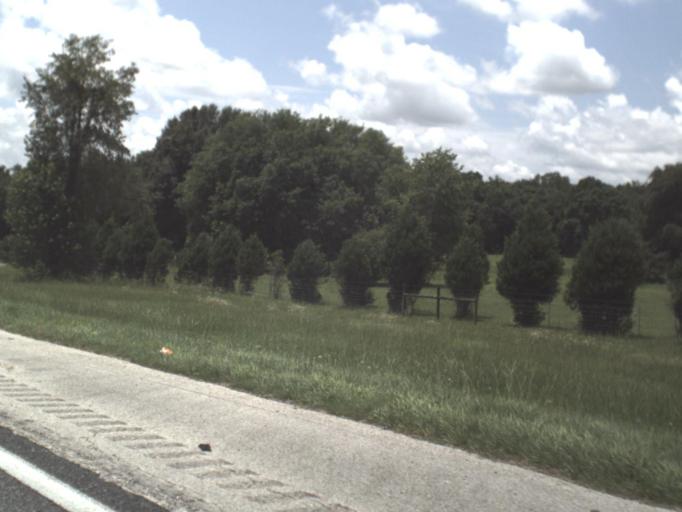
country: US
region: Florida
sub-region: Alachua County
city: High Springs
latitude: 29.8566
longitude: -82.5382
